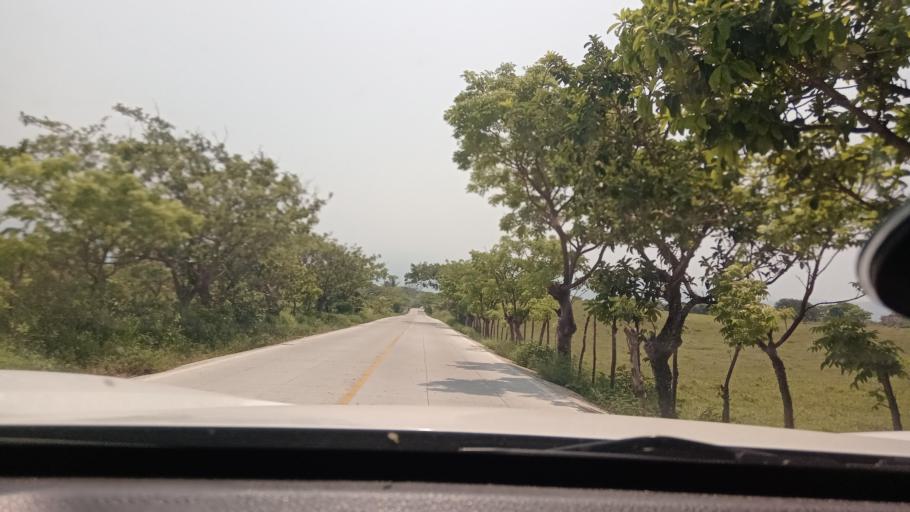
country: MX
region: Veracruz
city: Catemaco
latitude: 18.5579
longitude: -95.0085
